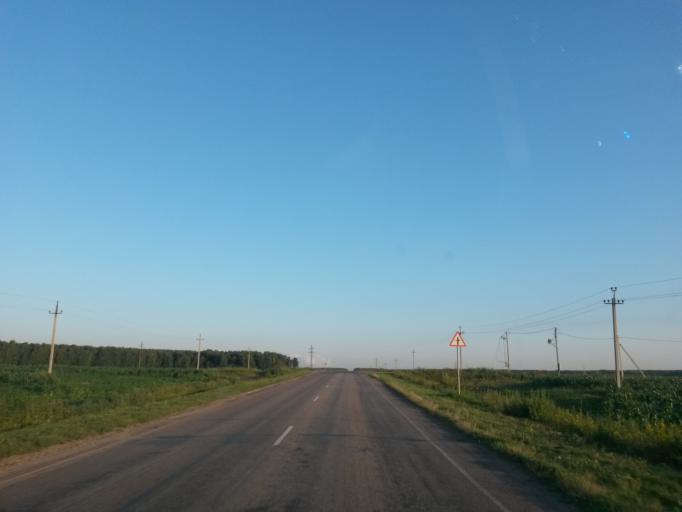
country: RU
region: Moskovskaya
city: Barybino
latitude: 55.2042
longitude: 37.7891
